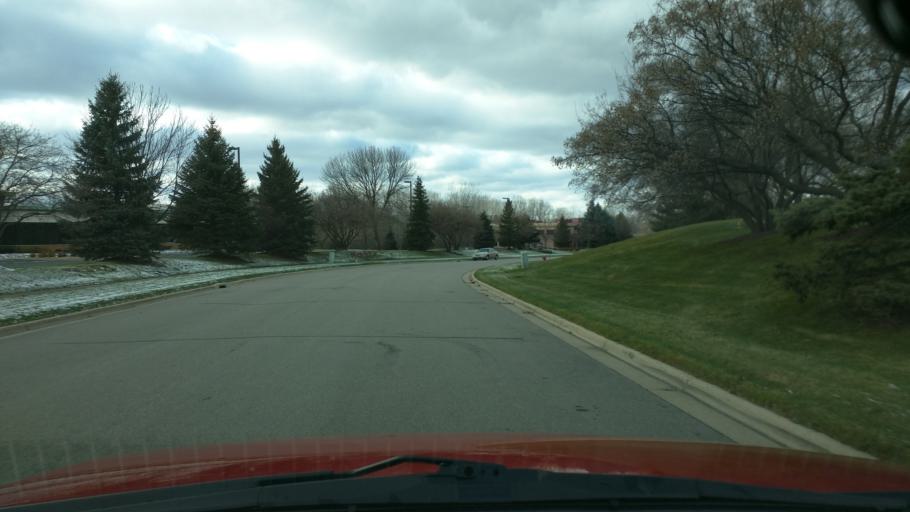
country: US
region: Minnesota
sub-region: Hennepin County
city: Eden Prairie
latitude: 44.8635
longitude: -93.4516
